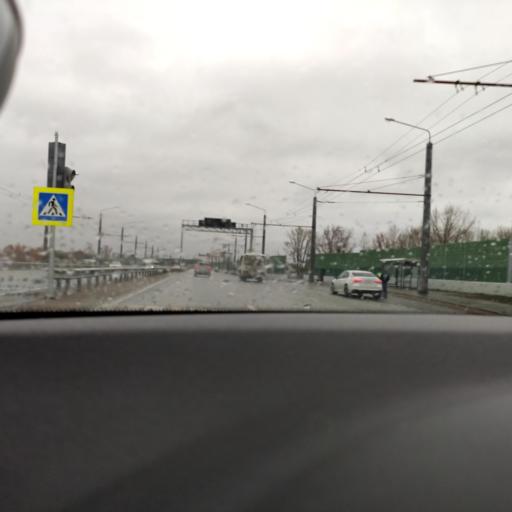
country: RU
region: Samara
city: Samara
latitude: 53.1605
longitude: 50.0898
